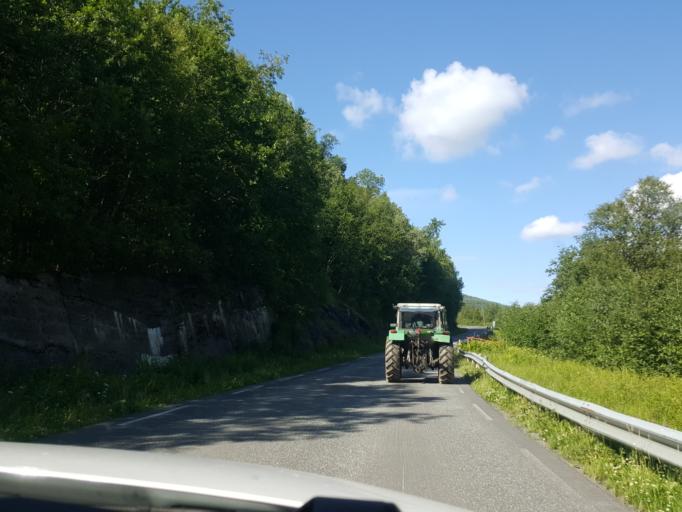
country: NO
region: Nordland
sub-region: Bodo
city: Loding
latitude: 67.1105
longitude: 15.0123
